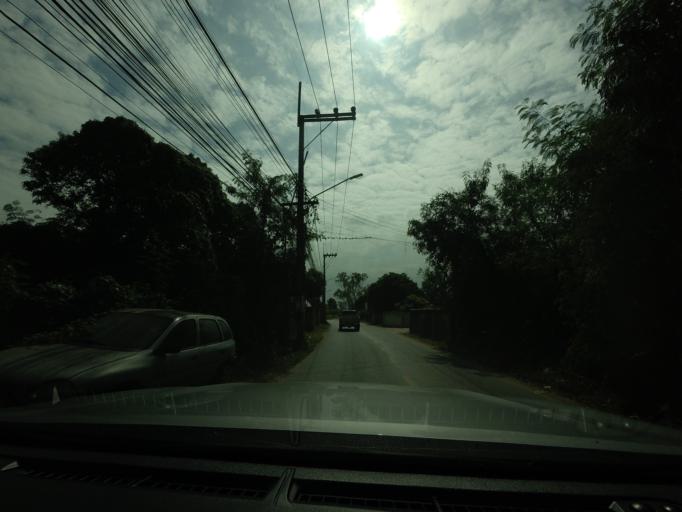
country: TH
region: Phitsanulok
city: Phitsanulok
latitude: 16.7977
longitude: 100.2457
